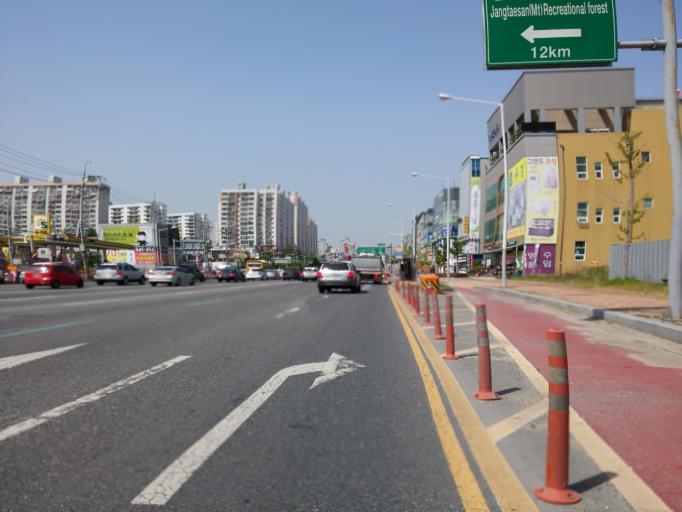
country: KR
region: Daejeon
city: Daejeon
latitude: 36.3057
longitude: 127.3550
